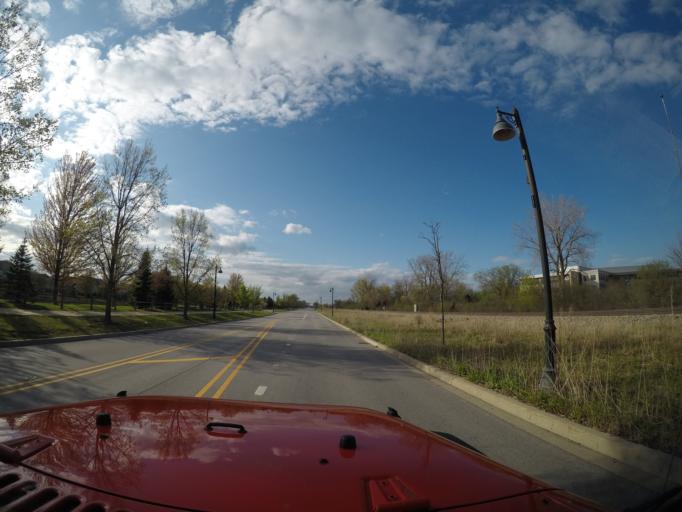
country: US
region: Illinois
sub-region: Cook County
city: Glenview
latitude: 42.0838
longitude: -87.8103
